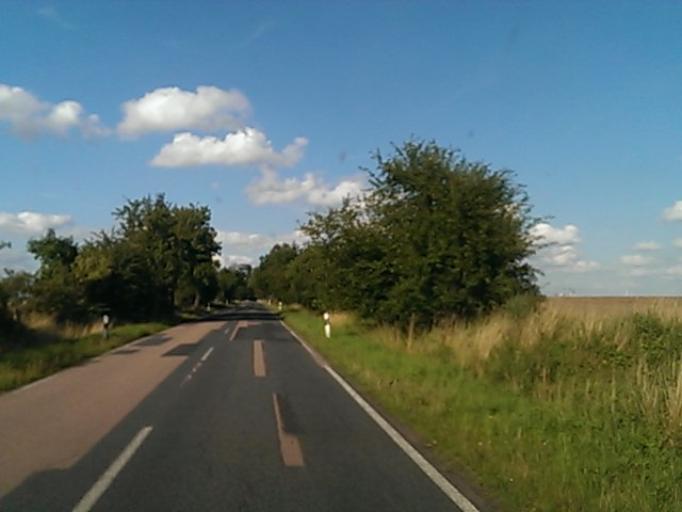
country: DE
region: Saxony-Anhalt
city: Nudersdorf
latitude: 51.9648
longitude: 12.5482
